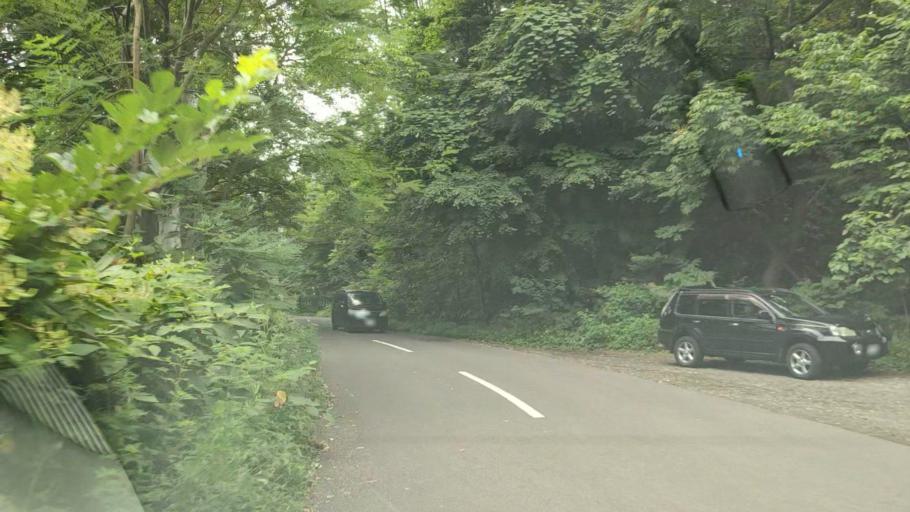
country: JP
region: Hokkaido
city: Otaru
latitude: 43.1930
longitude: 140.9848
